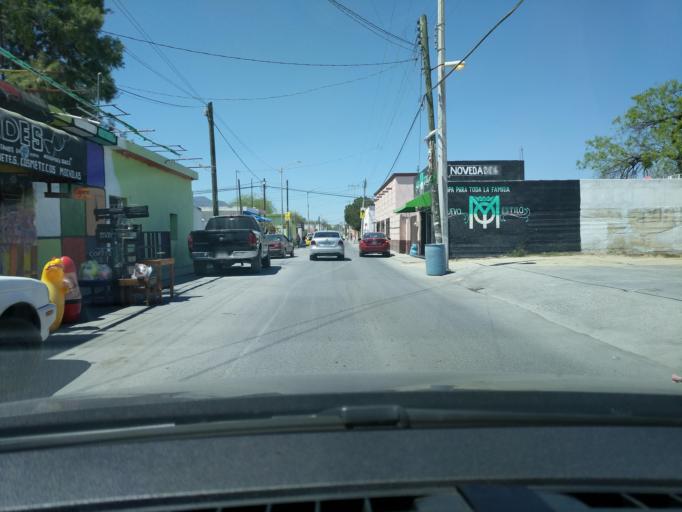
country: MX
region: Nuevo Leon
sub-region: Salinas Victoria
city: Las Torres
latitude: 25.9615
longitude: -100.2919
